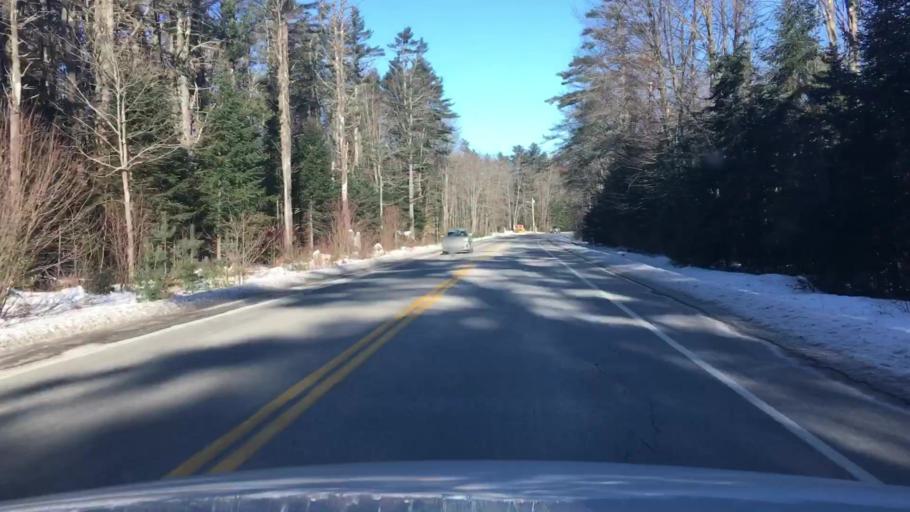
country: US
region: Maine
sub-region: Androscoggin County
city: Lisbon Falls
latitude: 43.9571
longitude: -70.1226
